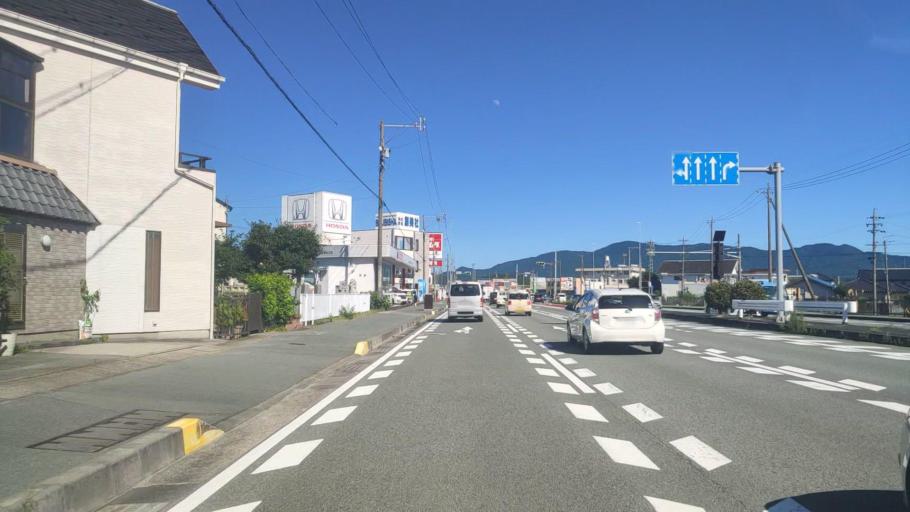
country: JP
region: Mie
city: Ise
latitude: 34.5074
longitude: 136.7253
